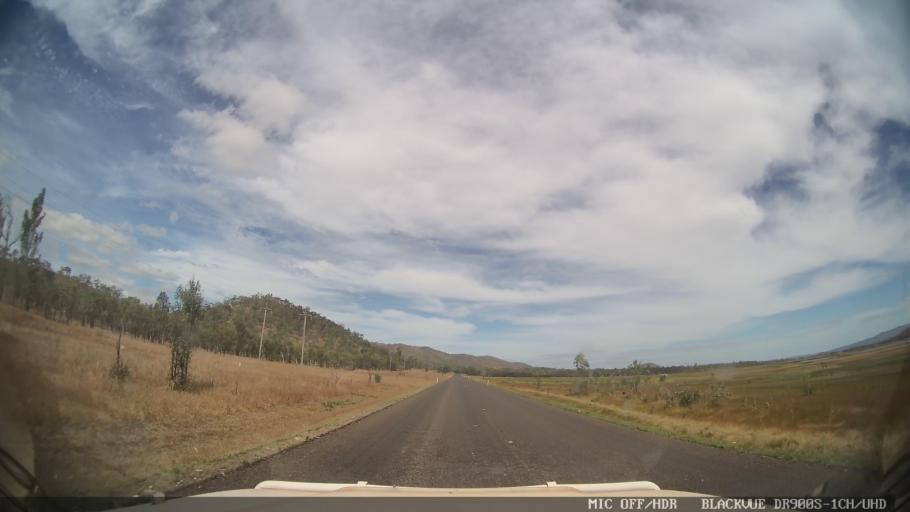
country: AU
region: Queensland
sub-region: Tablelands
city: Mareeba
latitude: -16.7908
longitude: 145.3551
